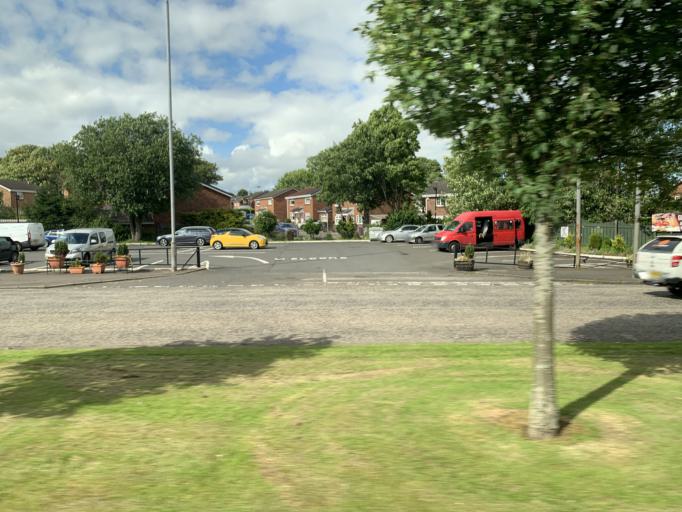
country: GB
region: Scotland
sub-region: South Lanarkshire
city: Uddingston
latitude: 55.8531
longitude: -4.1076
